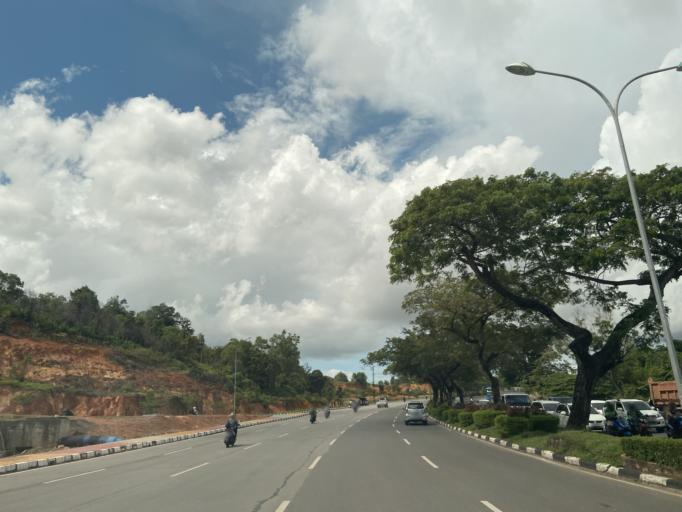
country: SG
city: Singapore
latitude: 1.1243
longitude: 104.0193
